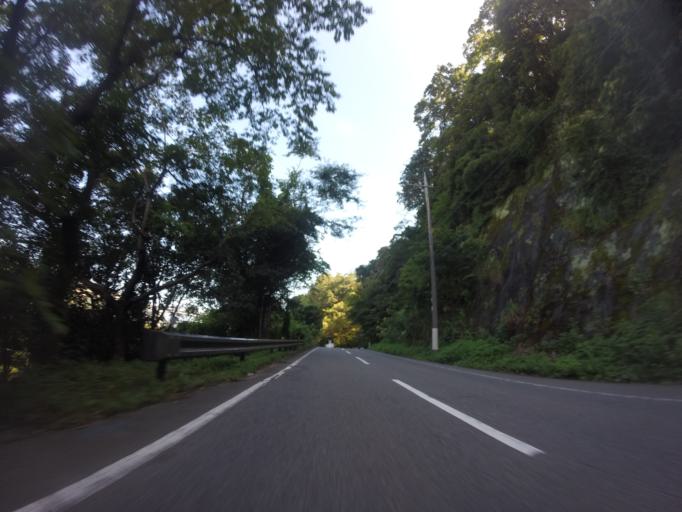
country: JP
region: Shizuoka
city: Fujinomiya
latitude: 35.3105
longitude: 138.4550
